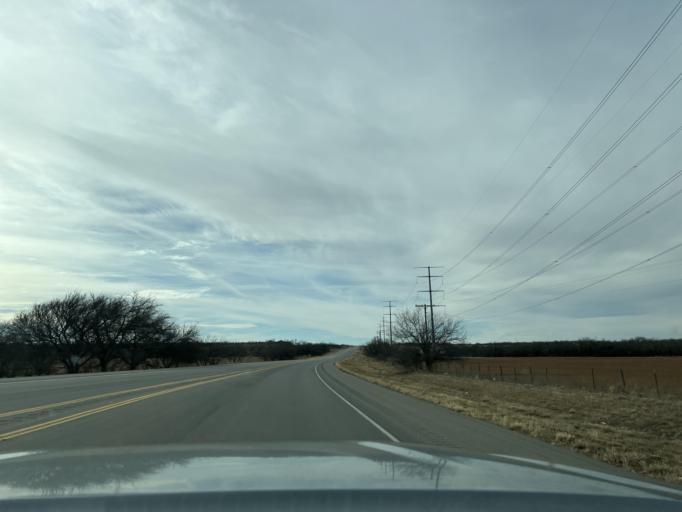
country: US
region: Texas
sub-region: Jones County
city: Stamford
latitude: 32.7504
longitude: -99.6311
